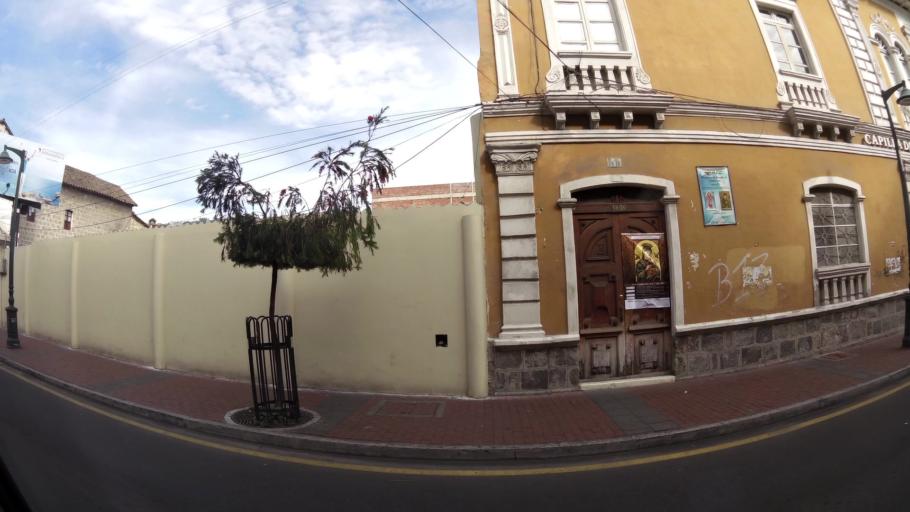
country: EC
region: Tungurahua
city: Ambato
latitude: -1.2457
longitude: -78.6285
